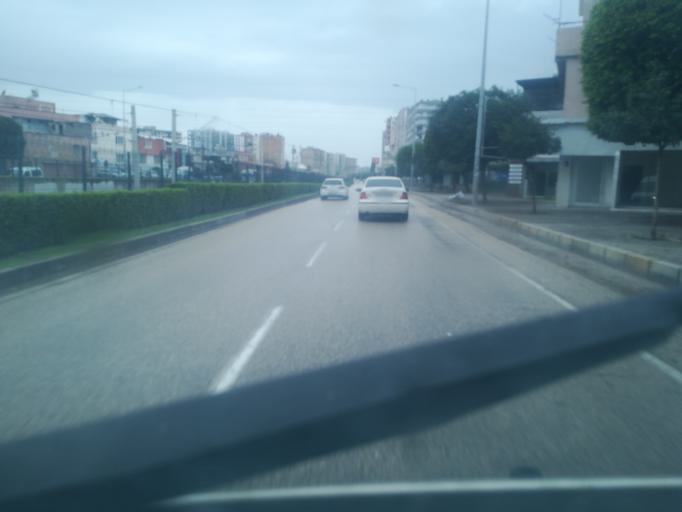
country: TR
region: Adana
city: Seyhan
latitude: 37.0053
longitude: 35.3102
